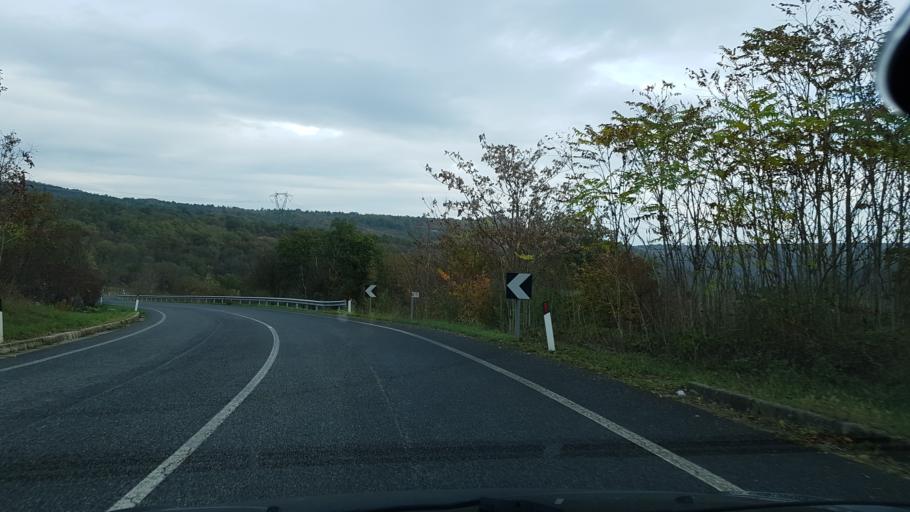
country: IT
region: Friuli Venezia Giulia
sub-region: Provincia di Gorizia
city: Doberdo del Lago
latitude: 45.8667
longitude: 13.5589
